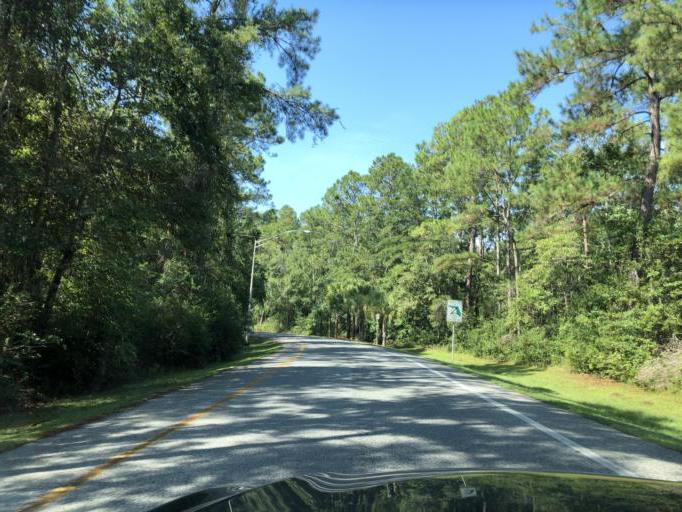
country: US
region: Florida
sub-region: Walton County
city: DeFuniak Springs
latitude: 30.7134
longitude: -85.9324
